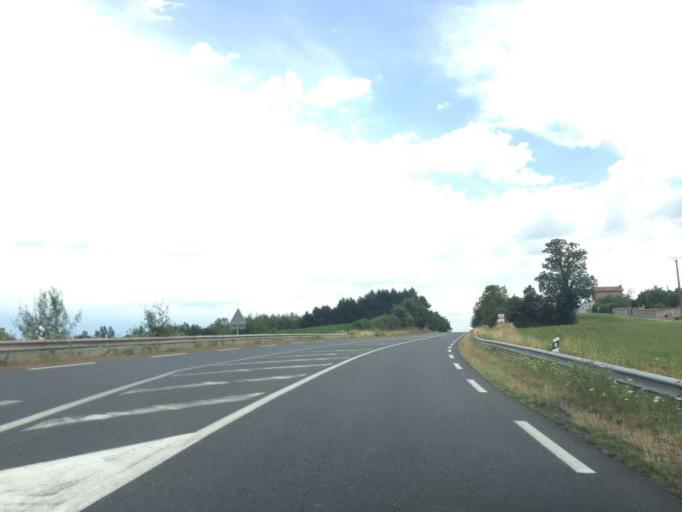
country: FR
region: Rhone-Alpes
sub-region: Departement de la Loire
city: Saint-Symphorien-de-Lay
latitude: 45.9518
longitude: 4.1972
